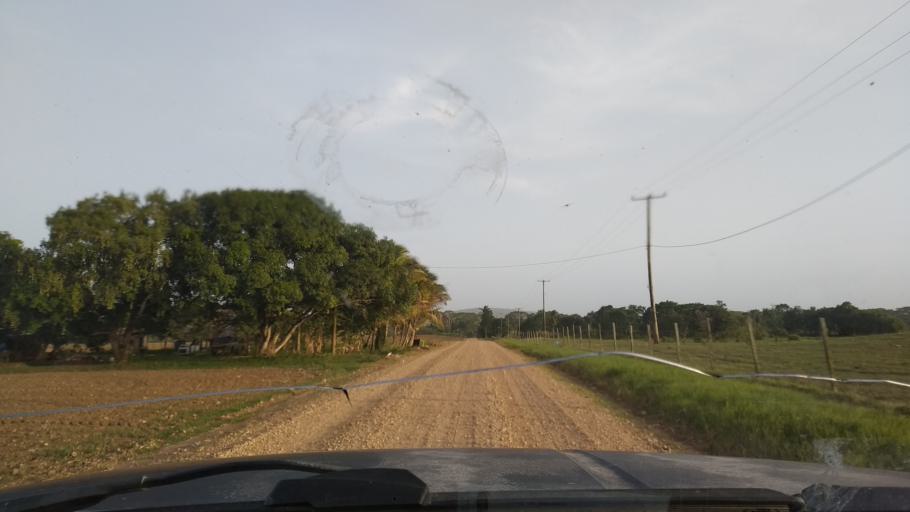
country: BZ
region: Cayo
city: San Ignacio
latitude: 17.2118
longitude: -89.0137
